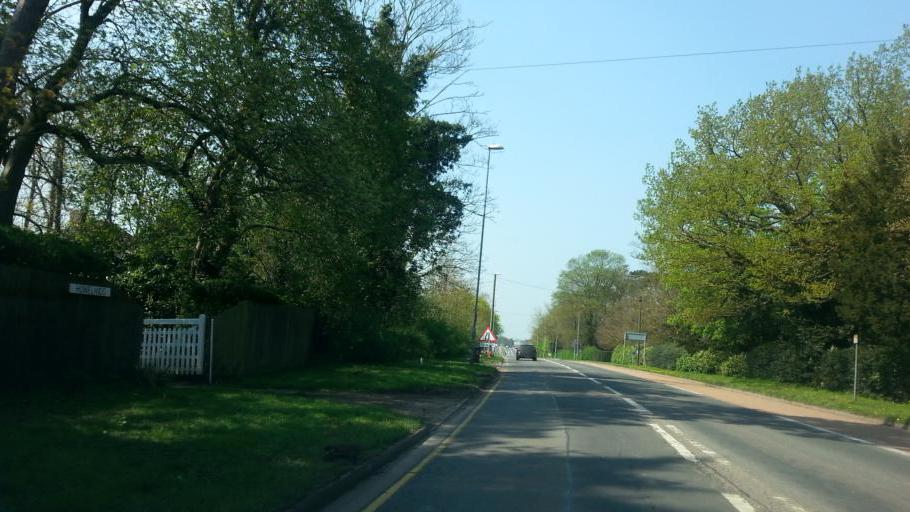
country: GB
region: England
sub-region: Cambridgeshire
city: Girton
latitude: 52.2279
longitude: 0.0826
